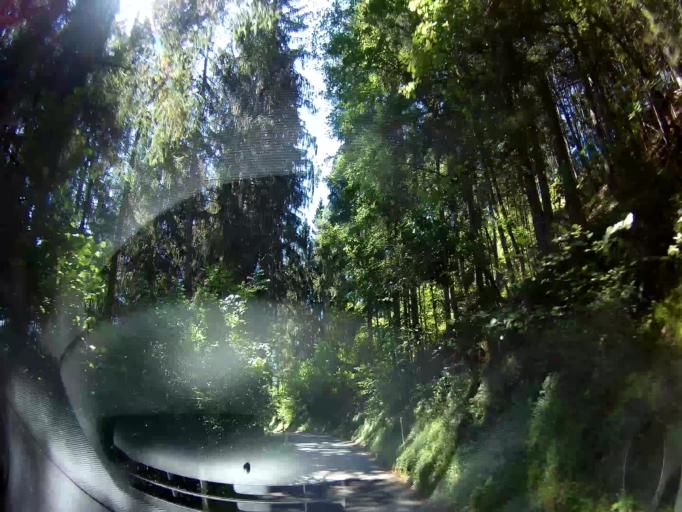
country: AT
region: Carinthia
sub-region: Politischer Bezirk Spittal an der Drau
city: Lendorf
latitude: 46.8225
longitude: 13.4428
